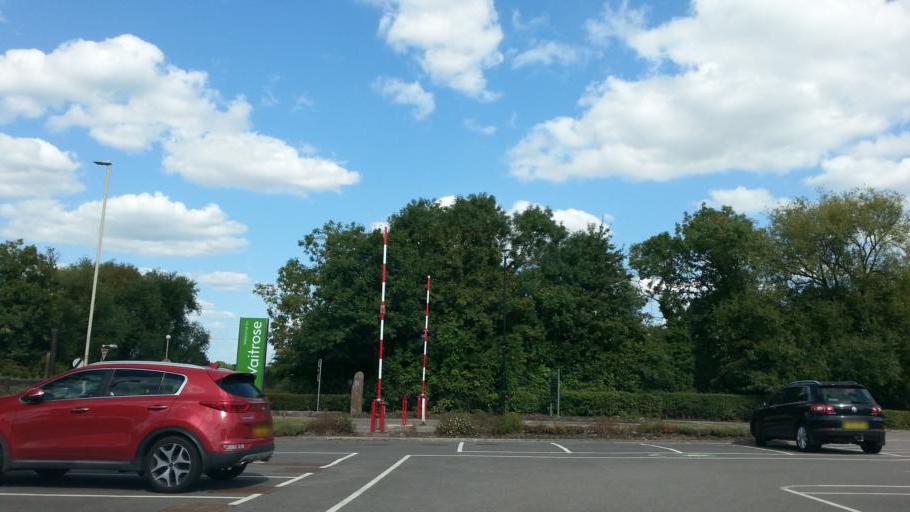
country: GB
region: England
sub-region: Leicestershire
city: Barrow upon Soar
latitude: 52.7374
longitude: -1.1497
